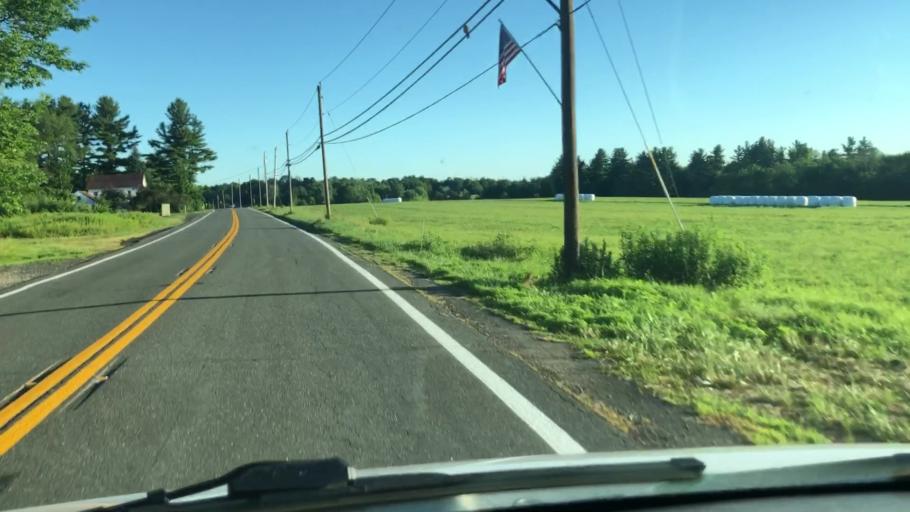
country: US
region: Massachusetts
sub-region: Hampshire County
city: Chesterfield
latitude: 42.3885
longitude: -72.9308
